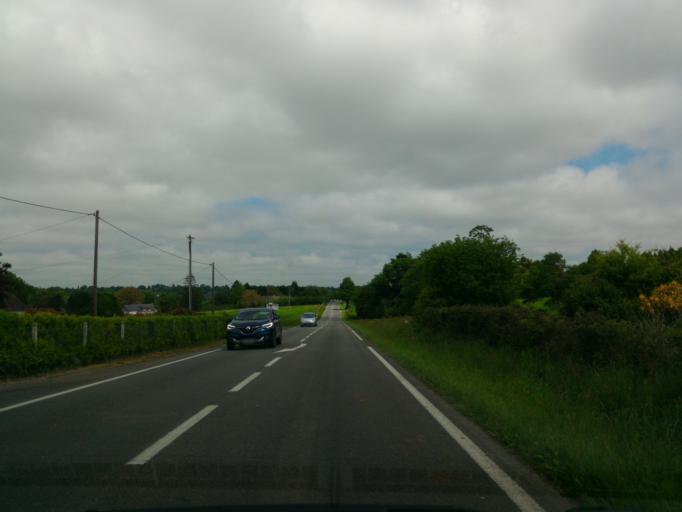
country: FR
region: Lower Normandy
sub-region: Departement de la Manche
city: Villedieu-les-Poeles
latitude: 48.8624
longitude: -1.2058
